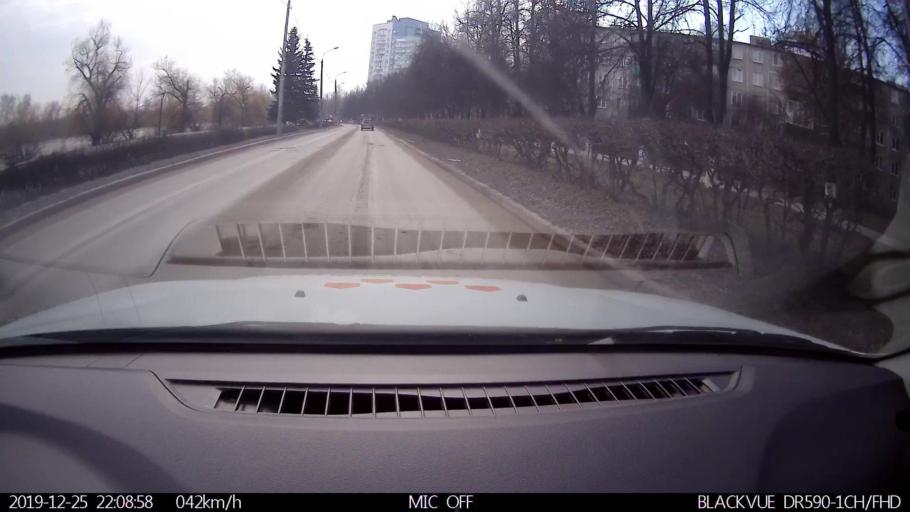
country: RU
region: Nizjnij Novgorod
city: Gorbatovka
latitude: 56.3434
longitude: 43.8487
